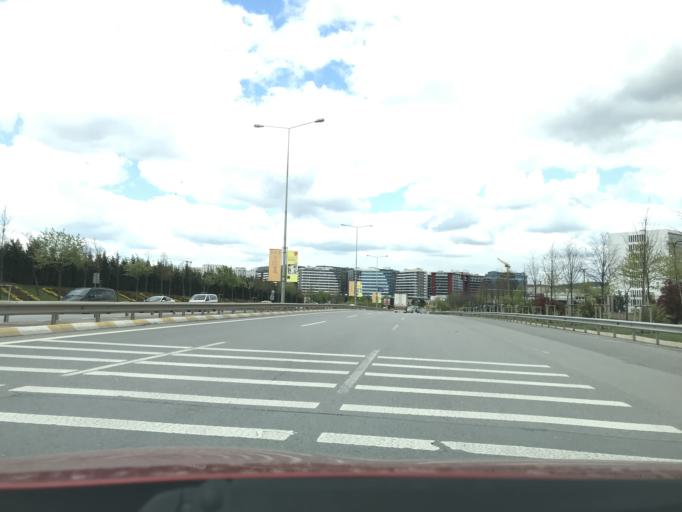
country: TR
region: Istanbul
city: Sultanbeyli
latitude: 40.9206
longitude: 29.3123
